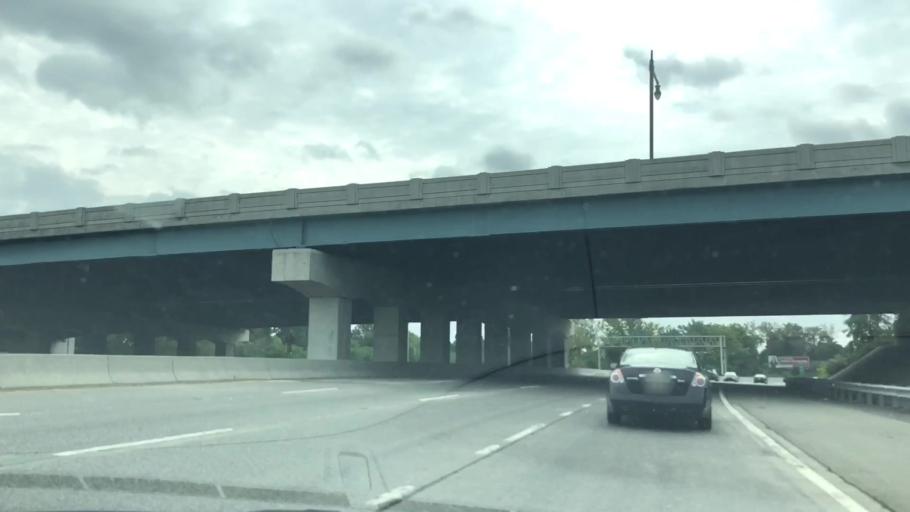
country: US
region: New Jersey
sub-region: Bergen County
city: Lyndhurst
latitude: 40.8239
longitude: -74.1246
